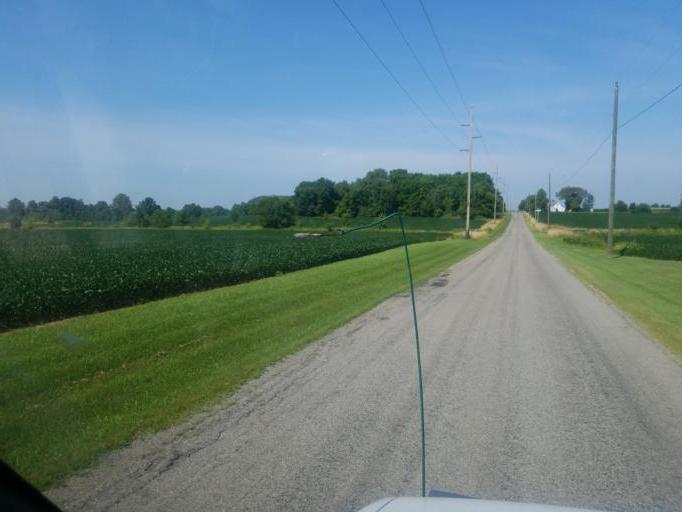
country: US
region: Ohio
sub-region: Union County
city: Marysville
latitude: 40.2882
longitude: -83.3630
